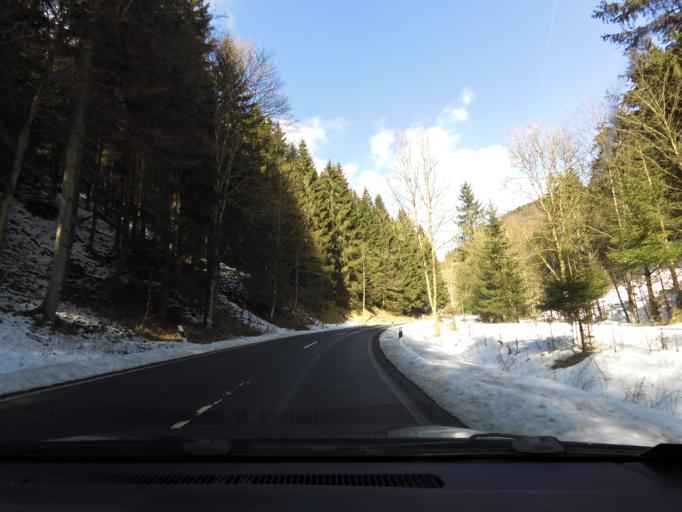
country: DE
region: Lower Saxony
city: Sankt Andreasberg
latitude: 51.6804
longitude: 10.4985
